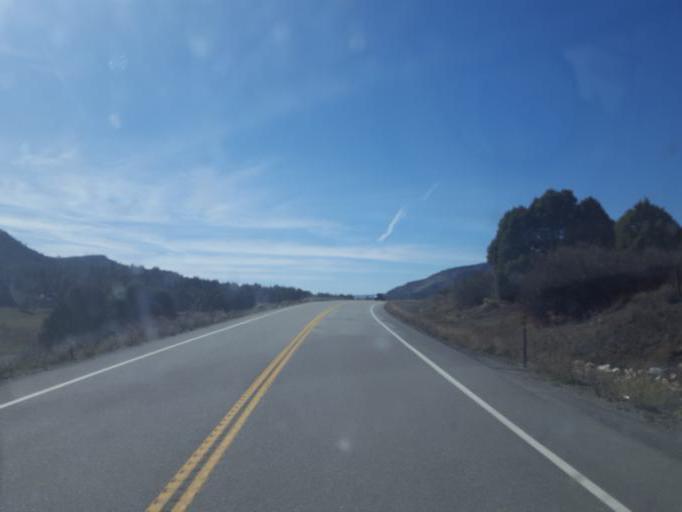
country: US
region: Colorado
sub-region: Archuleta County
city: Pagosa Springs
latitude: 37.2296
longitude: -107.1916
